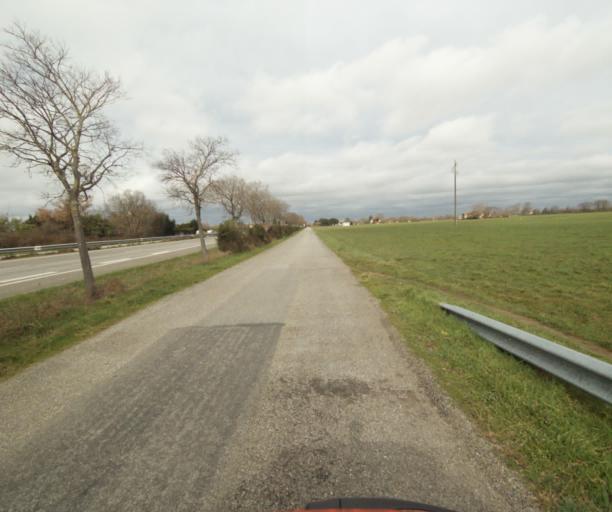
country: FR
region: Midi-Pyrenees
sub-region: Departement de l'Ariege
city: La Tour-du-Crieu
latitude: 43.1191
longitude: 1.6301
